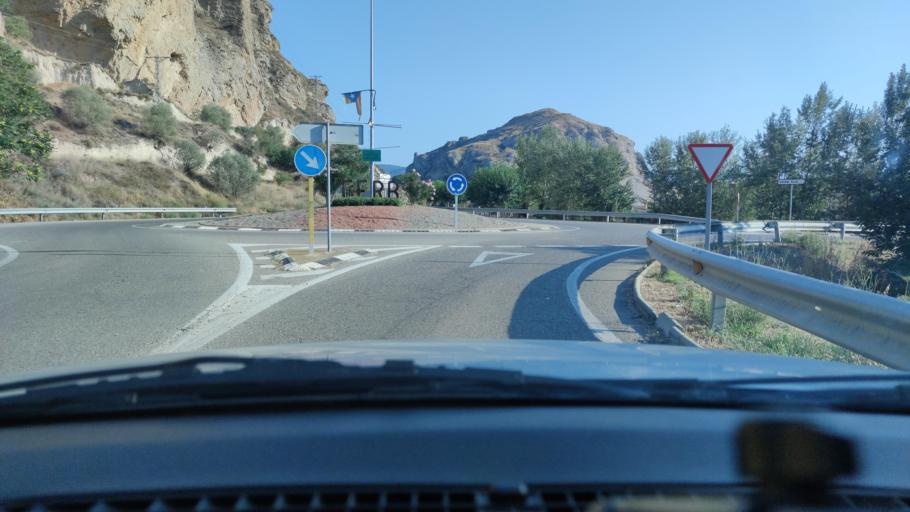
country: ES
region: Catalonia
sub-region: Provincia de Lleida
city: Balaguer
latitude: 41.8194
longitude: 0.8037
